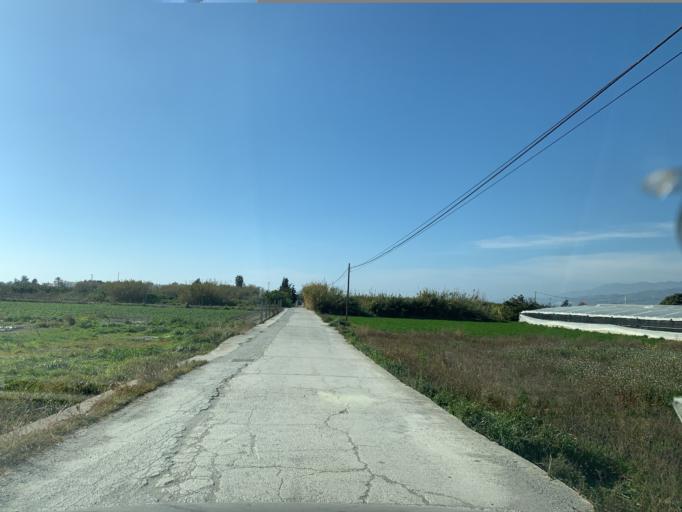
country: ES
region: Andalusia
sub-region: Provincia de Granada
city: El Varadero
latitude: 36.7260
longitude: -3.5548
